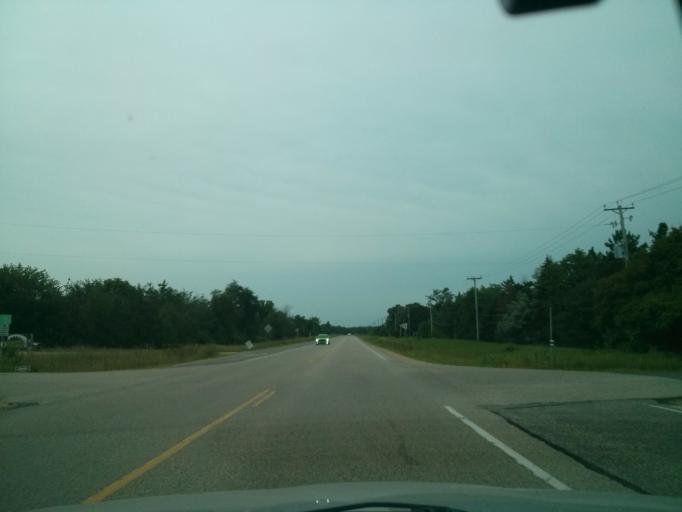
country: US
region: Minnesota
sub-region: Washington County
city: Lakeland
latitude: 44.9389
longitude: -92.7711
